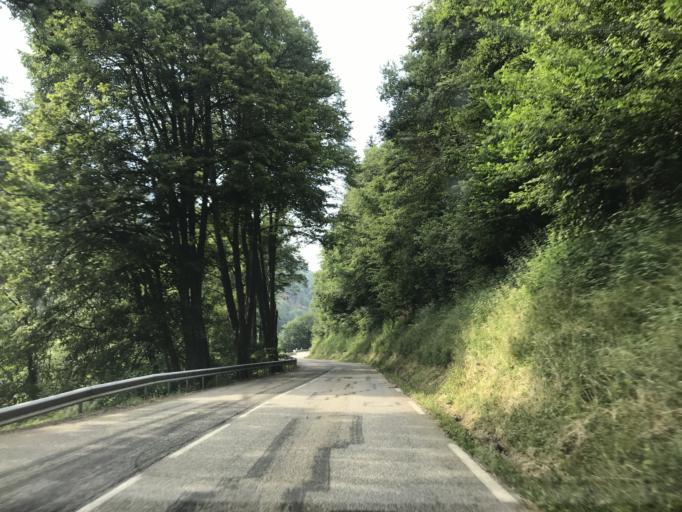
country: FR
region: Rhone-Alpes
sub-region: Departement de l'Isere
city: Allevard
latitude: 45.3606
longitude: 6.0988
